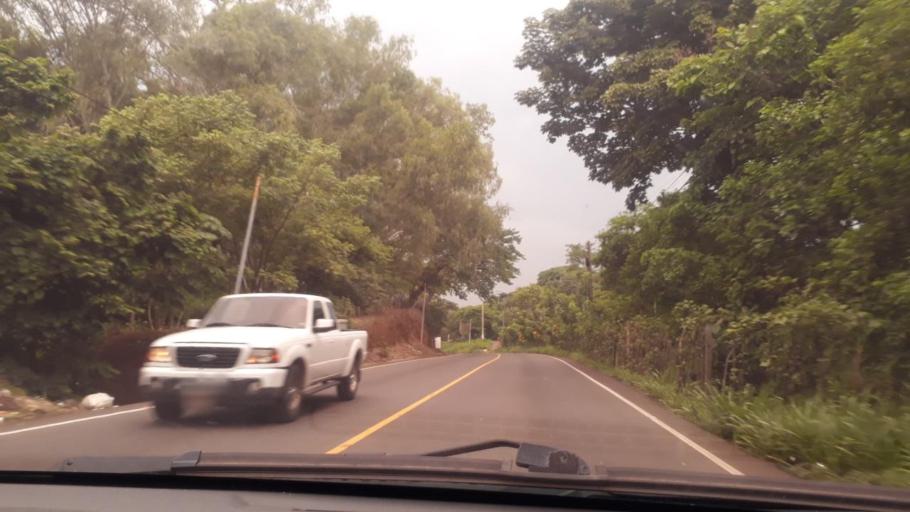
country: GT
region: Santa Rosa
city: Guazacapan
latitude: 14.0718
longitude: -90.4255
